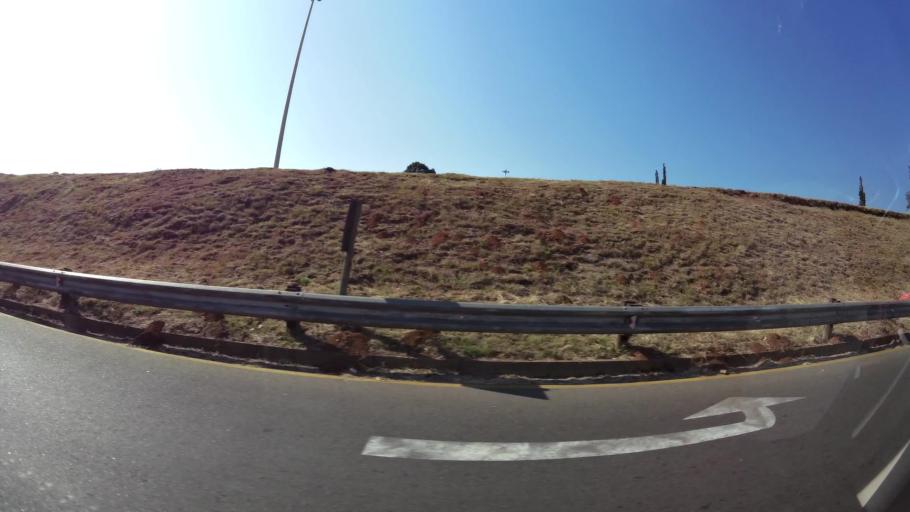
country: ZA
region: Gauteng
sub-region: City of Johannesburg Metropolitan Municipality
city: Modderfontein
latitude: -26.1329
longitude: 28.2244
